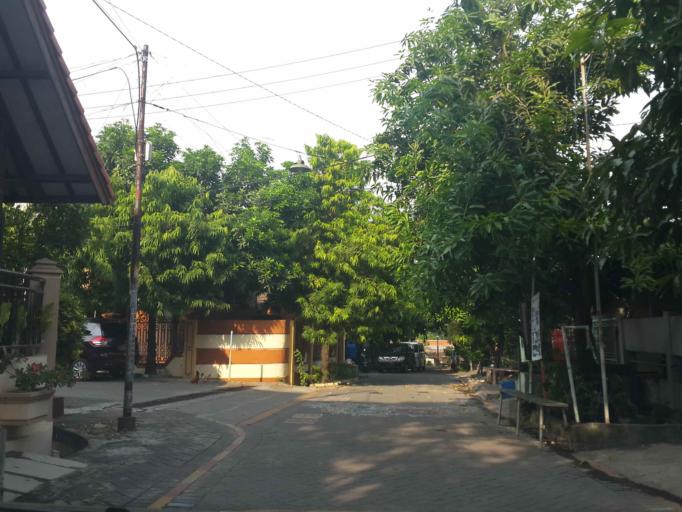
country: ID
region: East Java
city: Gresik
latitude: -7.1692
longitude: 112.6600
